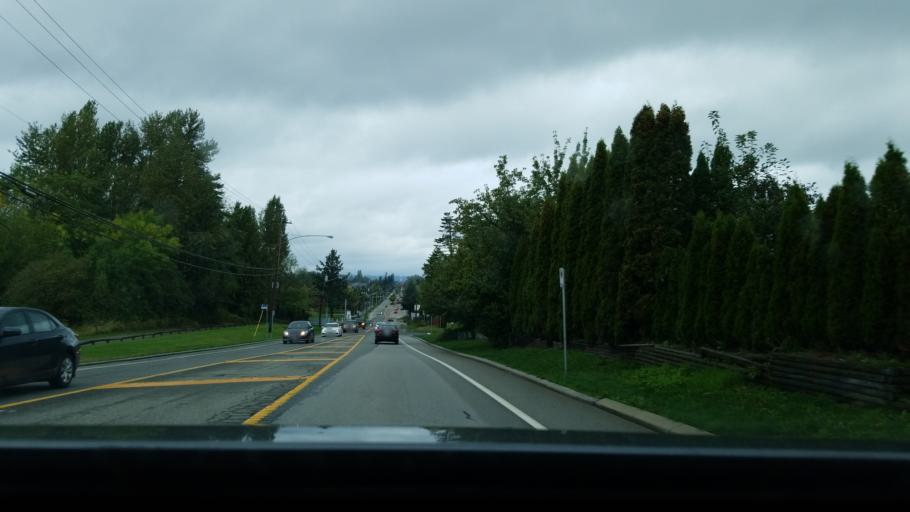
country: CA
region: British Columbia
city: Langley
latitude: 49.1188
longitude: -122.7247
